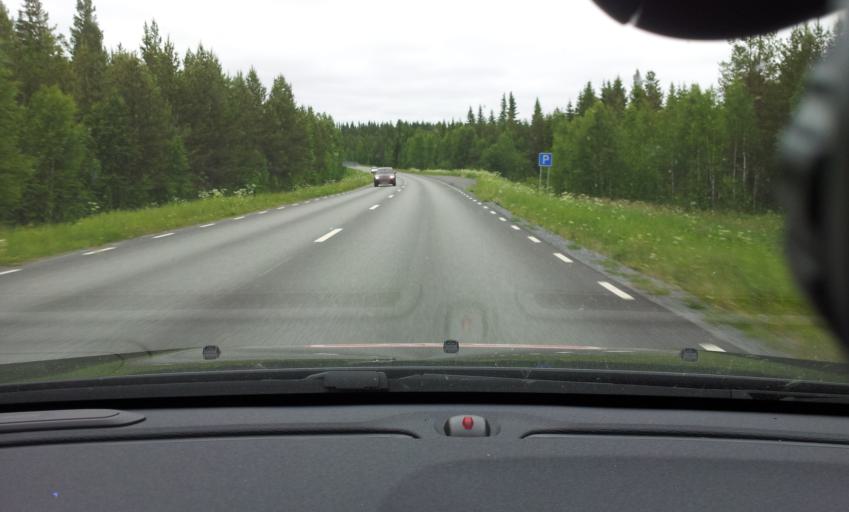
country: SE
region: Jaemtland
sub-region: Krokoms Kommun
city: Krokom
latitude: 63.0918
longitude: 14.3010
